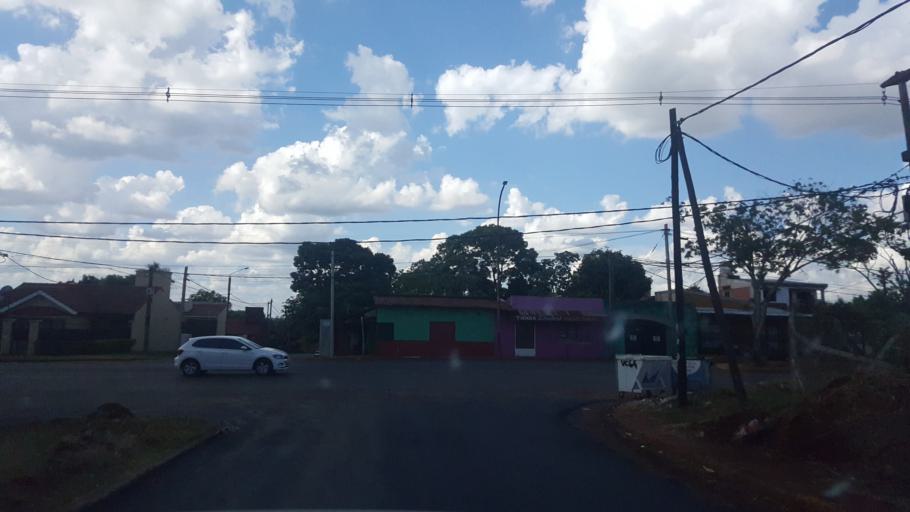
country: AR
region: Misiones
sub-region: Departamento de Capital
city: Posadas
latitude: -27.3588
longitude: -55.9192
